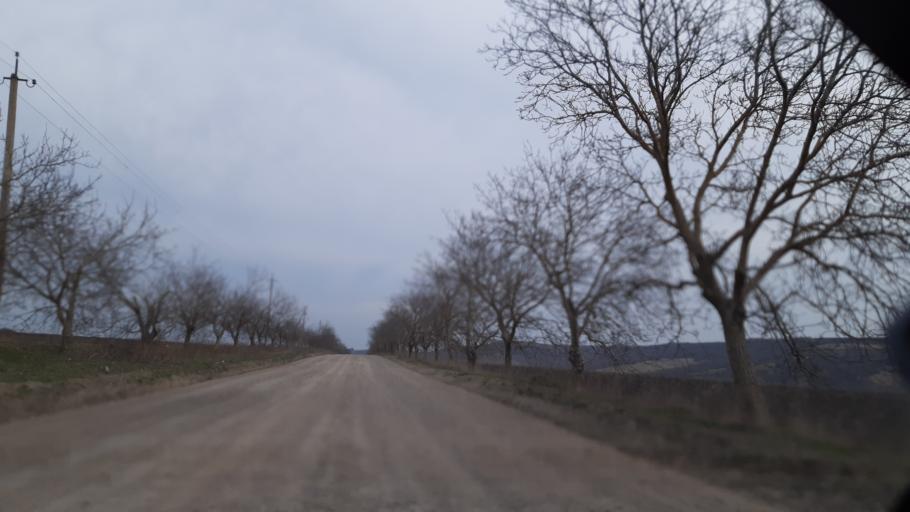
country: MD
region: Soldanesti
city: Soldanesti
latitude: 47.6942
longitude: 28.7343
